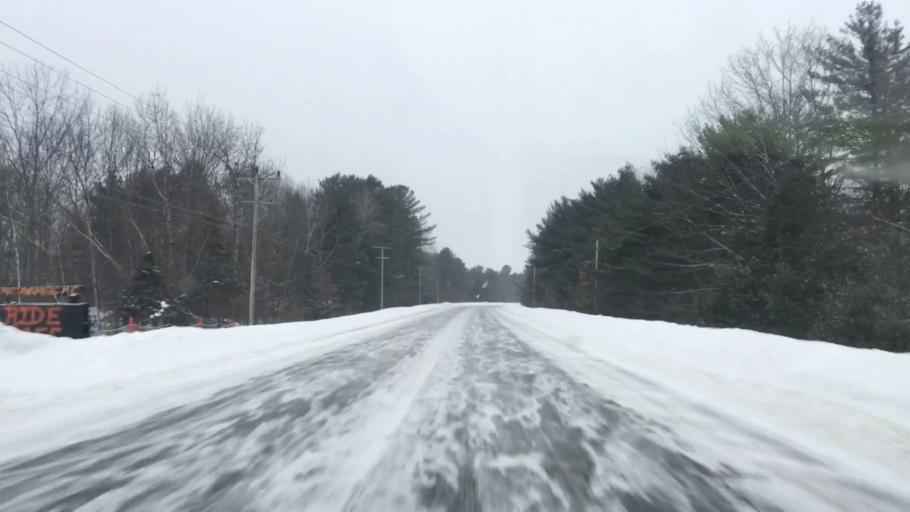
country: US
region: Maine
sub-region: Penobscot County
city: Medway
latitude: 45.5632
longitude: -68.3960
